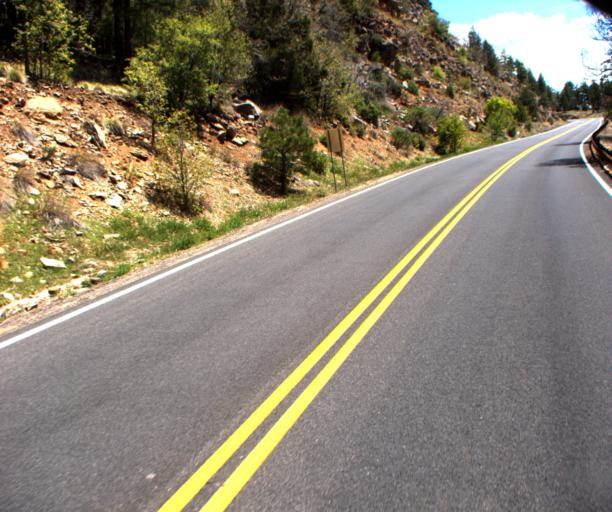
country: US
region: Arizona
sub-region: Coconino County
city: Kachina Village
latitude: 35.0295
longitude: -111.7388
